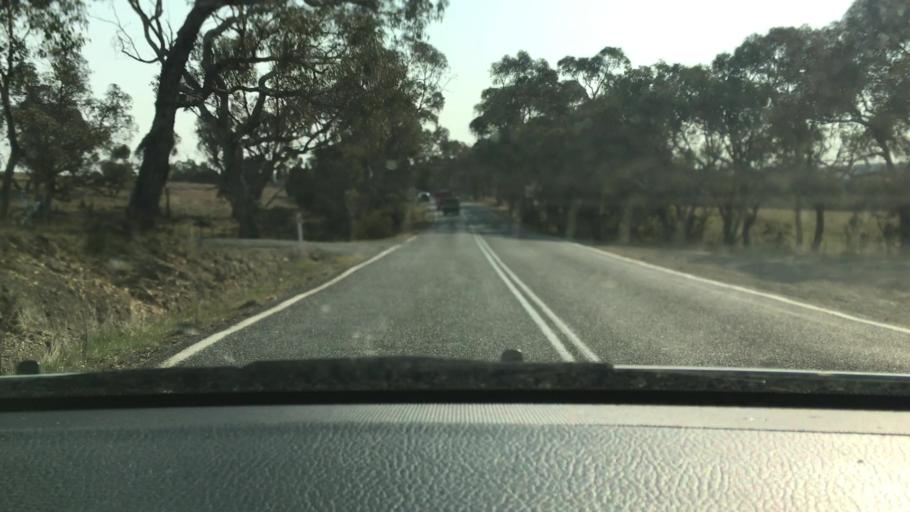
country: AU
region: New South Wales
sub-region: Queanbeyan
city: Queanbeyan
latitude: -35.4068
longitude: 149.2280
